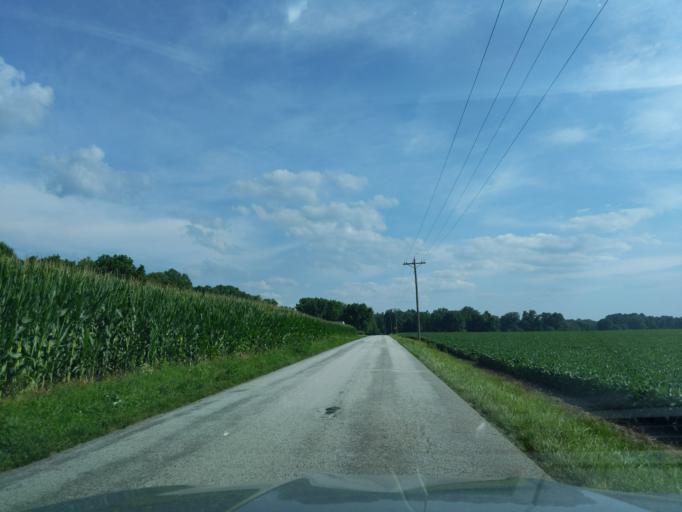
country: US
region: Indiana
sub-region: Decatur County
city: Greensburg
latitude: 39.2515
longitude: -85.4698
